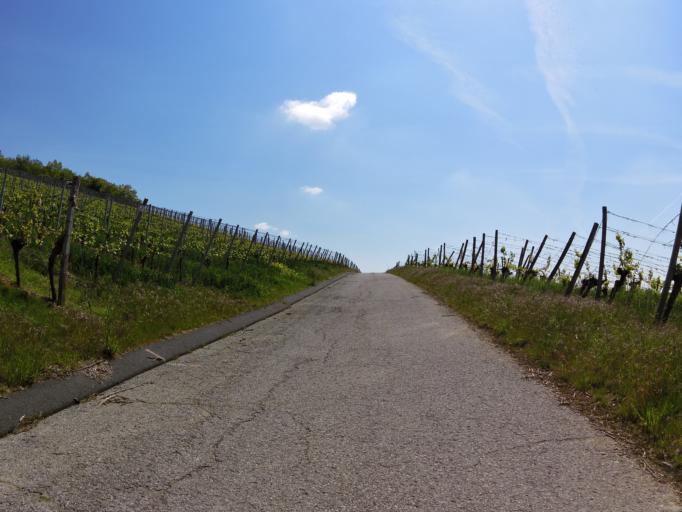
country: DE
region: Bavaria
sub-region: Regierungsbezirk Unterfranken
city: Eibelstadt
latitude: 49.7331
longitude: 10.0166
